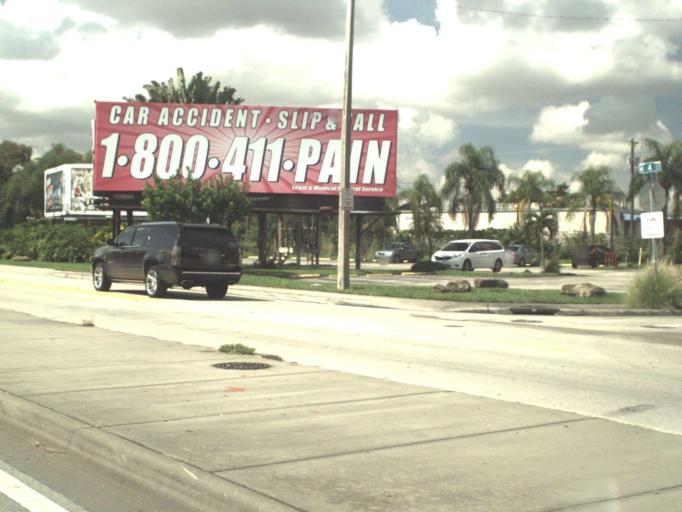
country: US
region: Florida
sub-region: Miami-Dade County
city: El Portal
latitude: 25.8269
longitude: -80.1870
